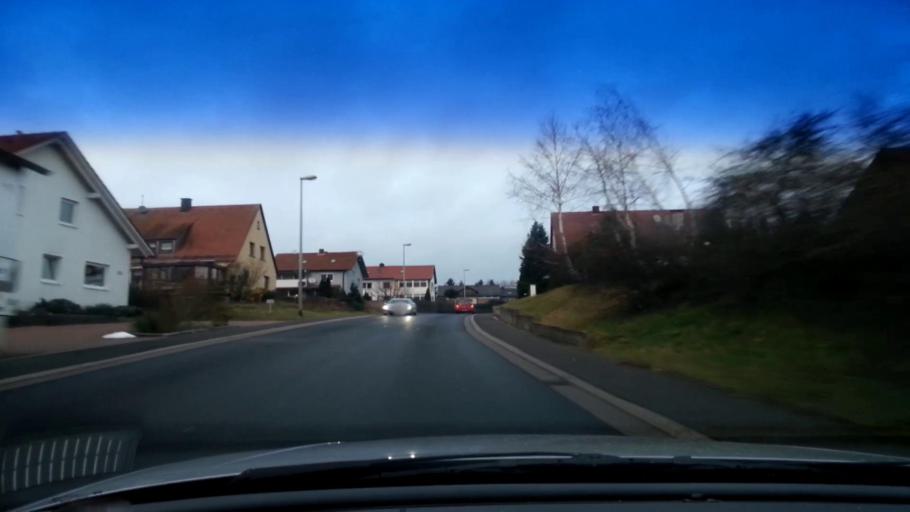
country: DE
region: Bavaria
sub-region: Upper Franconia
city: Walsdorf
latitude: 49.8726
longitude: 10.7801
